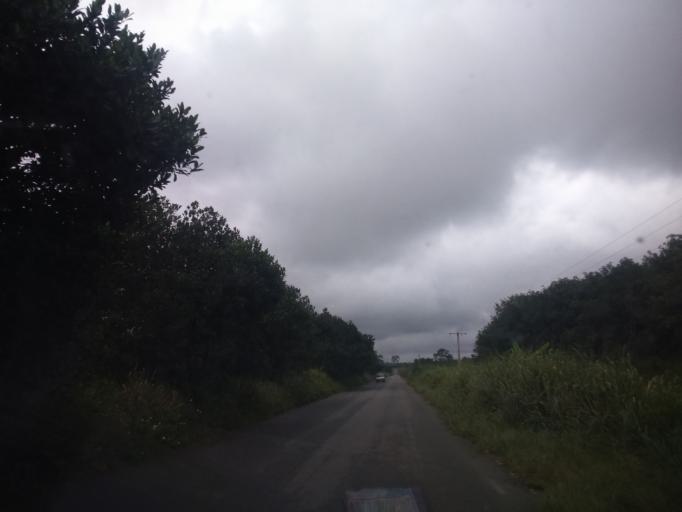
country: CI
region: Sud-Comoe
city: Adiake
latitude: 5.2922
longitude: -3.4488
